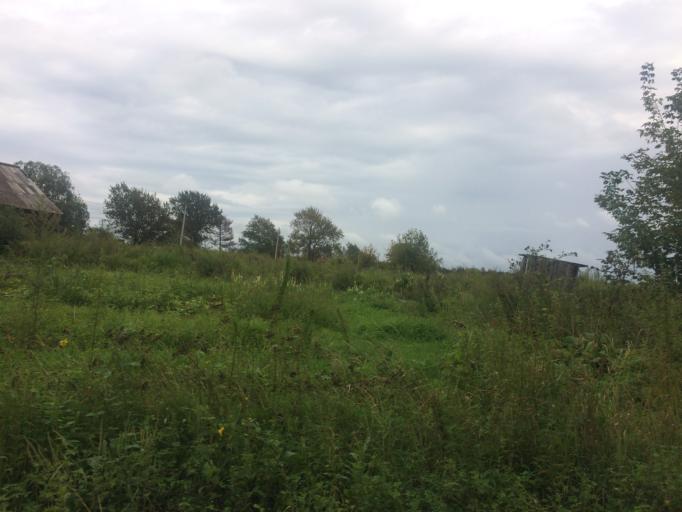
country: RU
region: Primorskiy
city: Lazo
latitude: 45.8306
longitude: 133.6158
